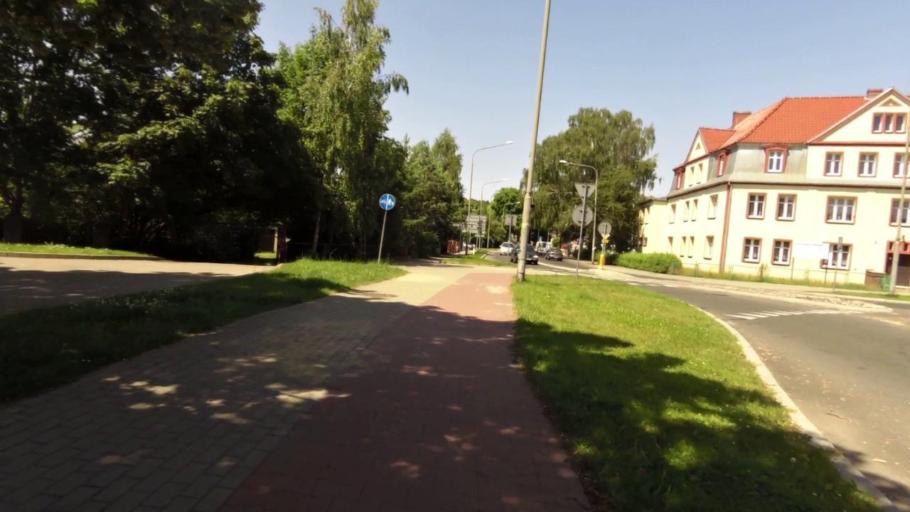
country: PL
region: West Pomeranian Voivodeship
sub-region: Powiat swidwinski
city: Polczyn-Zdroj
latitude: 53.7693
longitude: 16.0926
